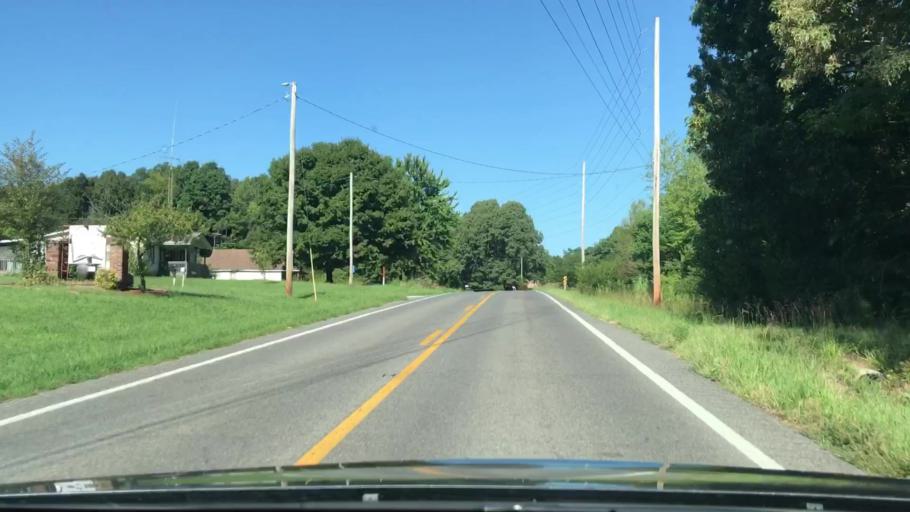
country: US
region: Kentucky
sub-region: Graves County
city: Mayfield
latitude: 36.7752
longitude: -88.4884
